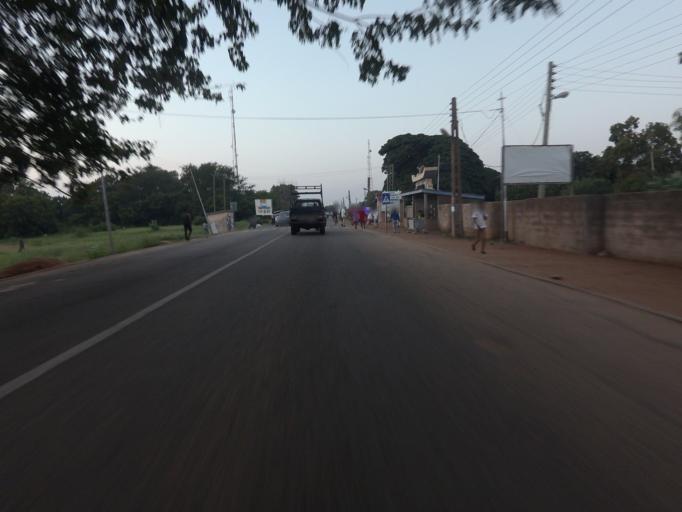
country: GH
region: Volta
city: Keta
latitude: 5.8955
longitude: 0.9870
